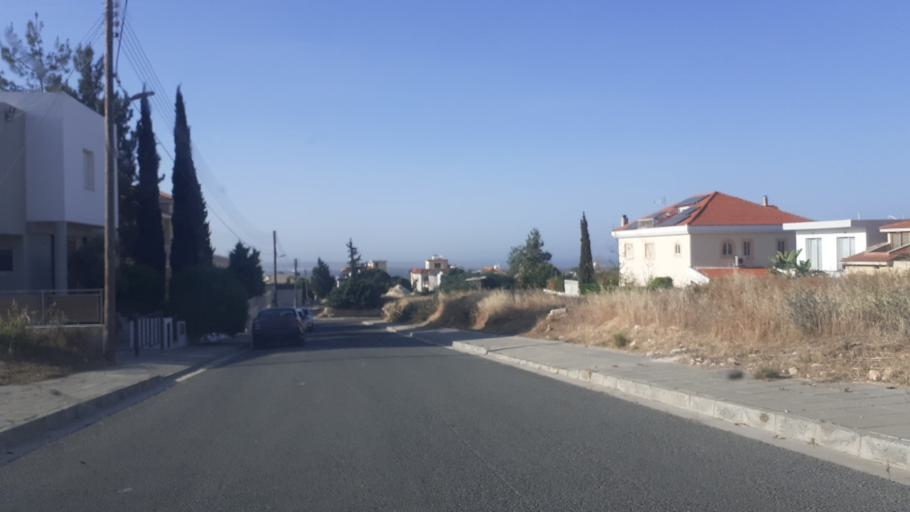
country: CY
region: Limassol
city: Ypsonas
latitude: 34.7027
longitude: 32.9406
